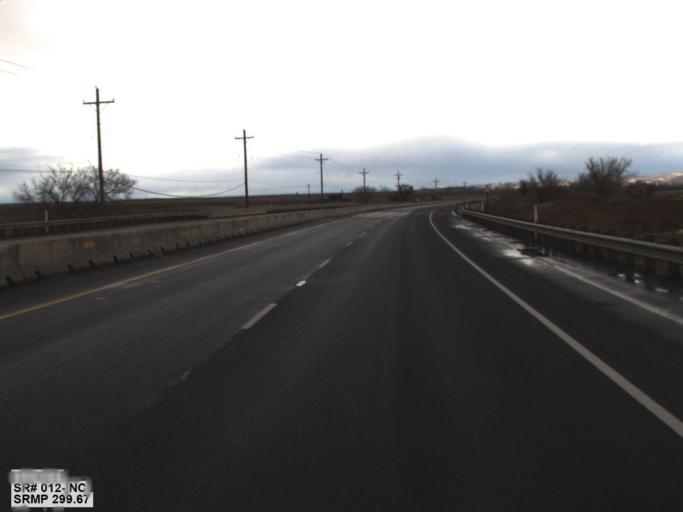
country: US
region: Washington
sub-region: Walla Walla County
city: Burbank
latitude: 46.1647
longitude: -118.9489
